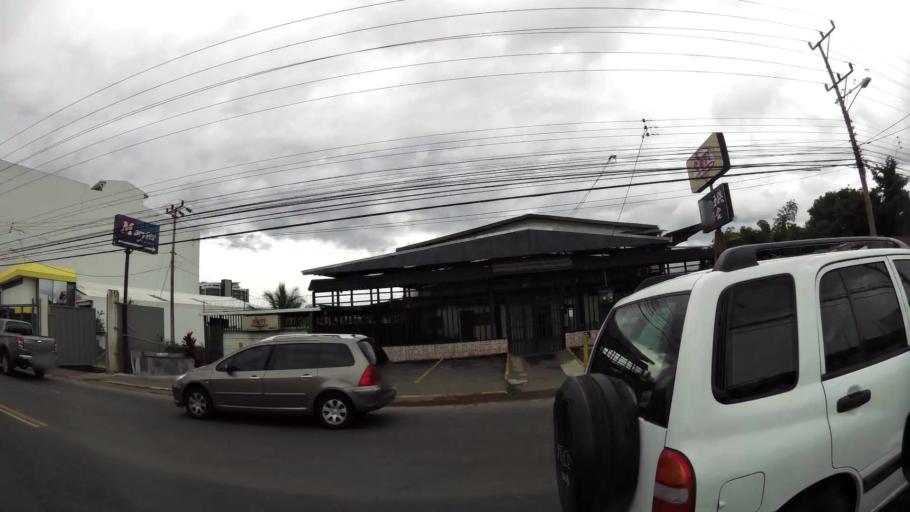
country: CR
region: San Jose
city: Colima
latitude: 9.9468
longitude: -84.0766
